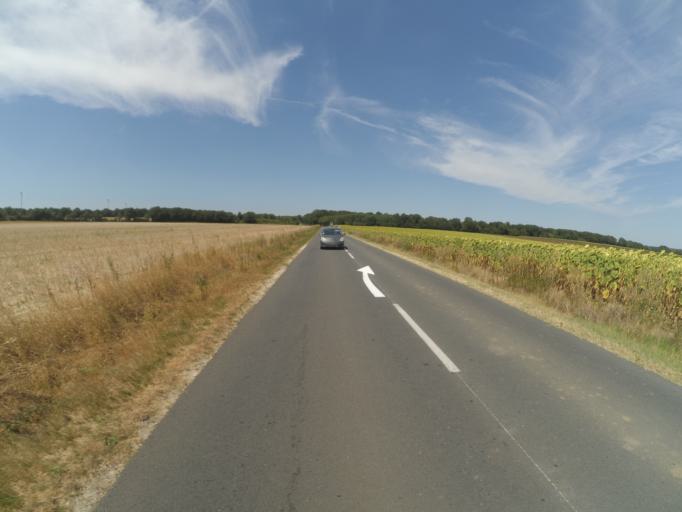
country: FR
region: Poitou-Charentes
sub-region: Departement de la Vienne
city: Saint-Maurice-la-Clouere
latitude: 46.3451
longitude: 0.4557
